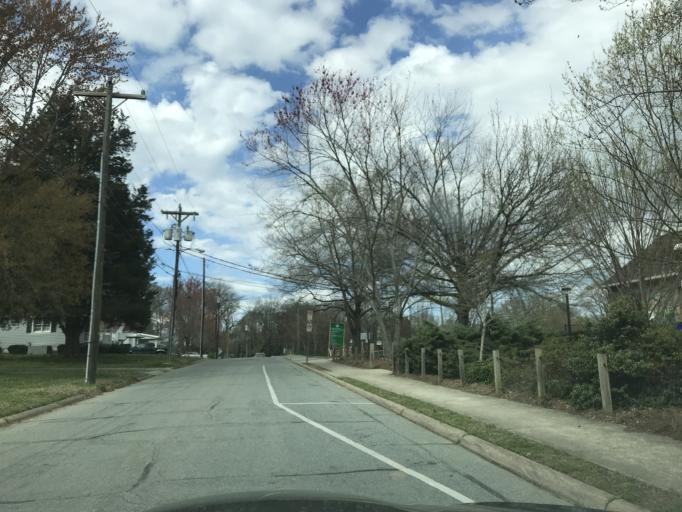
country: US
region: North Carolina
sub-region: Orange County
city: Chapel Hill
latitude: 35.9127
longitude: -79.0642
